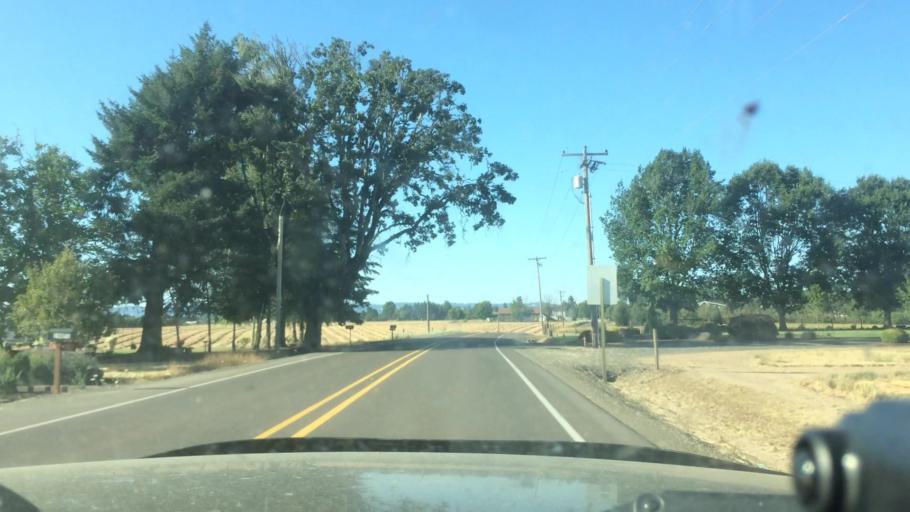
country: US
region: Oregon
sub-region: Yamhill County
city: Dundee
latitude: 45.2013
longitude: -122.9830
